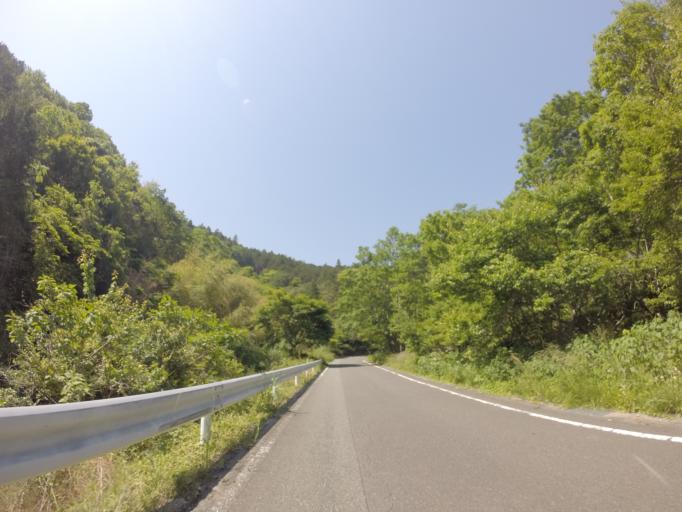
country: JP
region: Shizuoka
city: Fujinomiya
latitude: 35.1556
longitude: 138.5647
